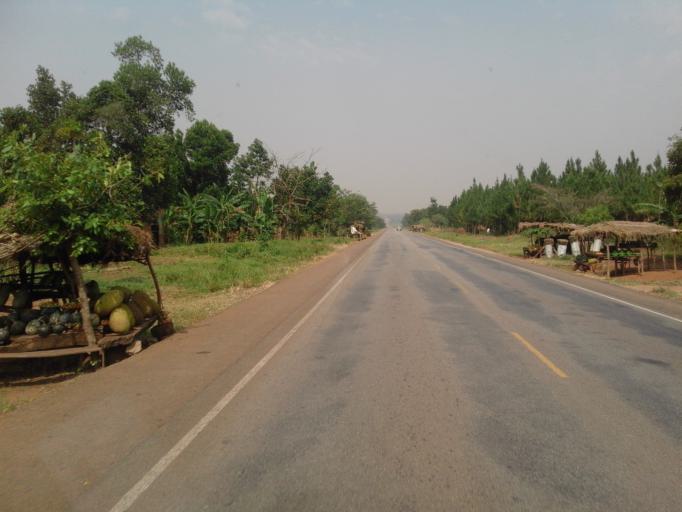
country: UG
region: Eastern Region
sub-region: Bugiri District
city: Bugiri
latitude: 0.6061
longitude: 33.6847
